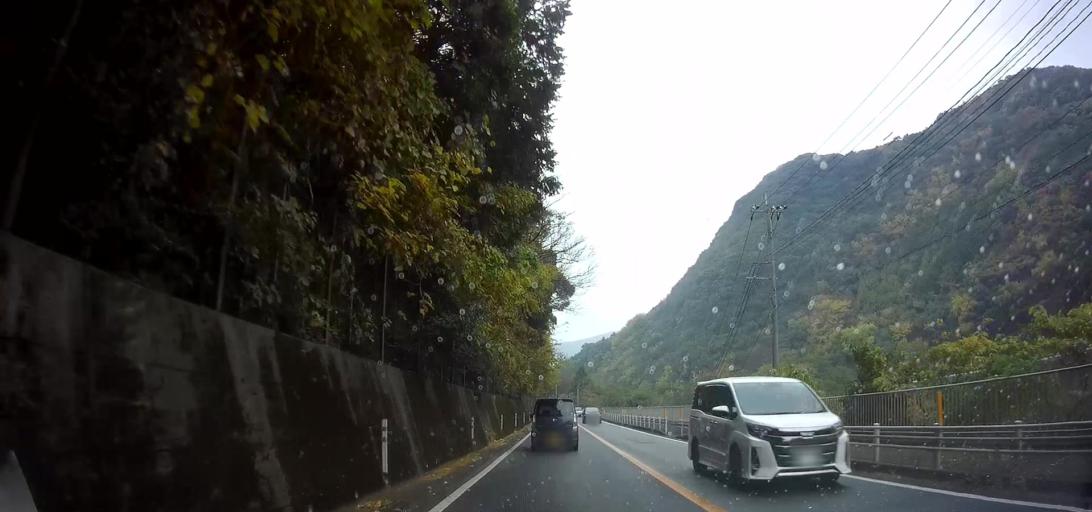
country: JP
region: Nagasaki
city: Shimabara
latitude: 32.7743
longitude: 130.2134
